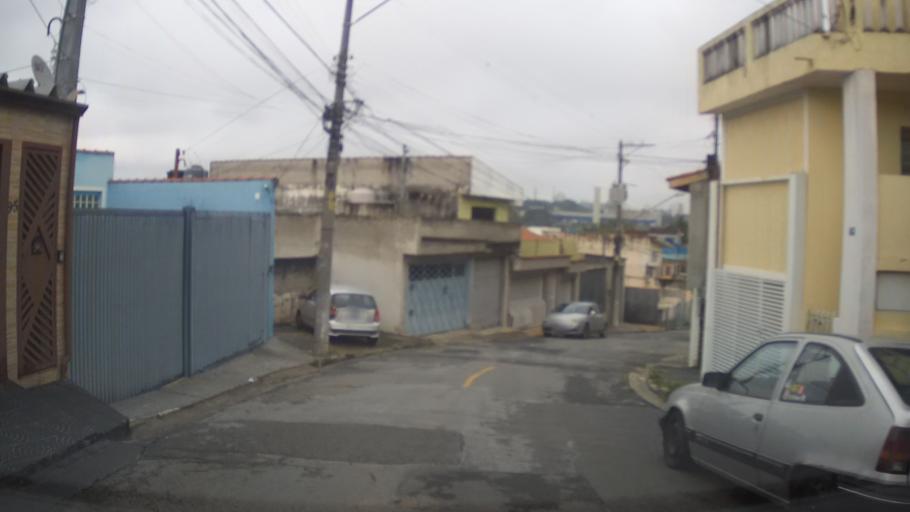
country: BR
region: Sao Paulo
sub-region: Guarulhos
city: Guarulhos
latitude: -23.4998
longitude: -46.5566
